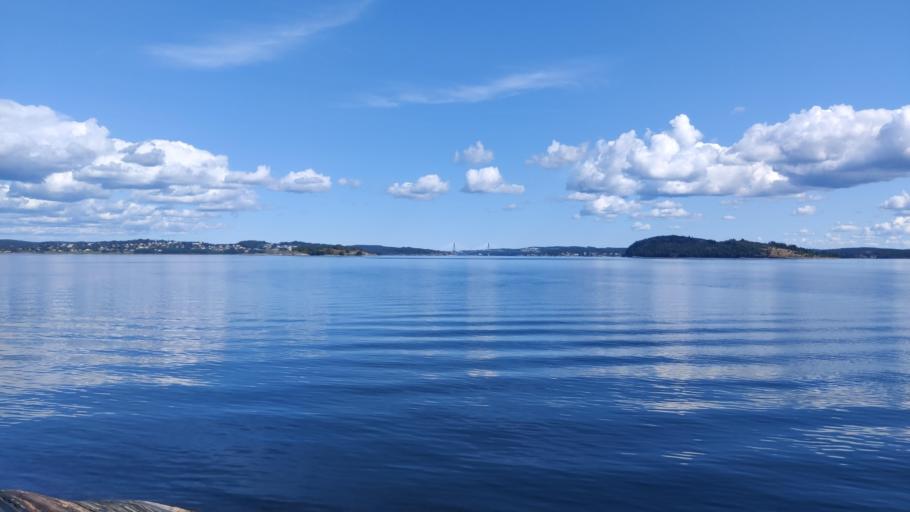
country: SE
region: Vaestra Goetaland
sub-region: Orust
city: Henan
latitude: 58.3078
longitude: 11.7298
